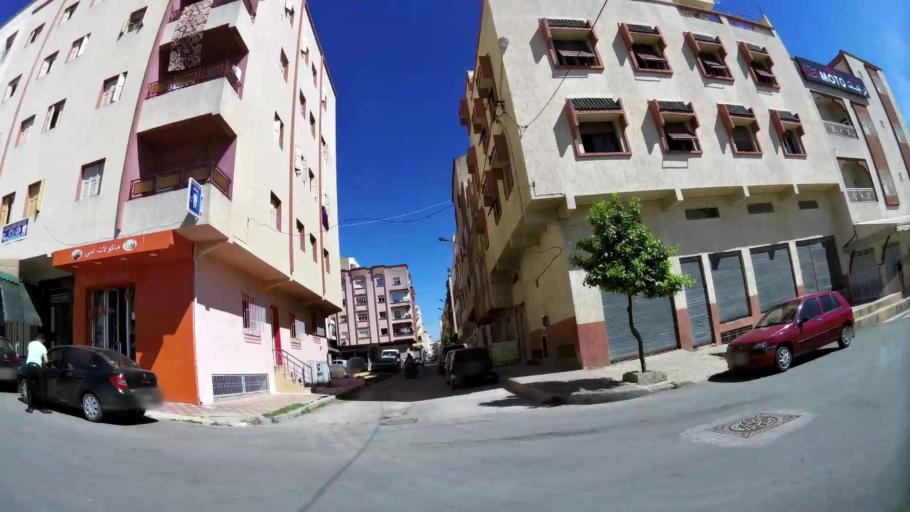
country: MA
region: Meknes-Tafilalet
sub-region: Meknes
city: Meknes
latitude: 33.8874
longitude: -5.5771
